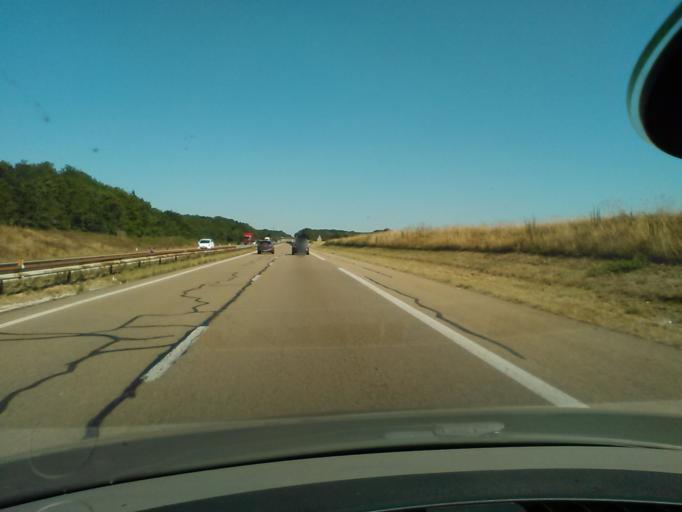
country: FR
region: Bourgogne
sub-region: Departement de l'Yonne
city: Vermenton
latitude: 47.7001
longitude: 3.8104
